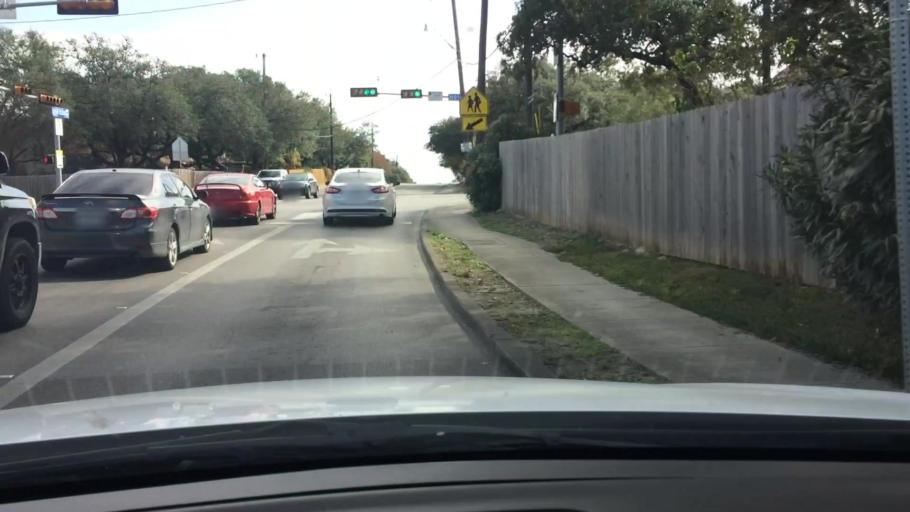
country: US
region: Texas
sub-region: Bexar County
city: Hollywood Park
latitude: 29.5759
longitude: -98.4681
